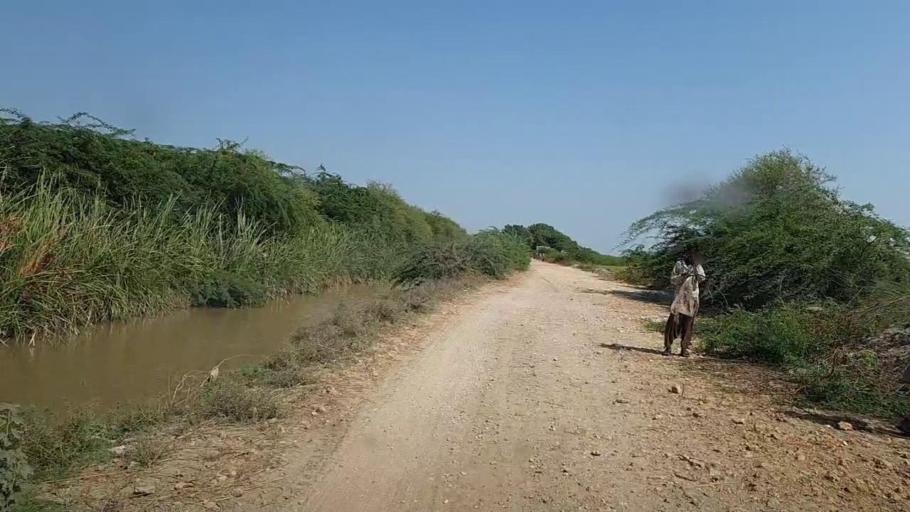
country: PK
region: Sindh
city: Mirpur Batoro
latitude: 24.7145
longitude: 68.4438
